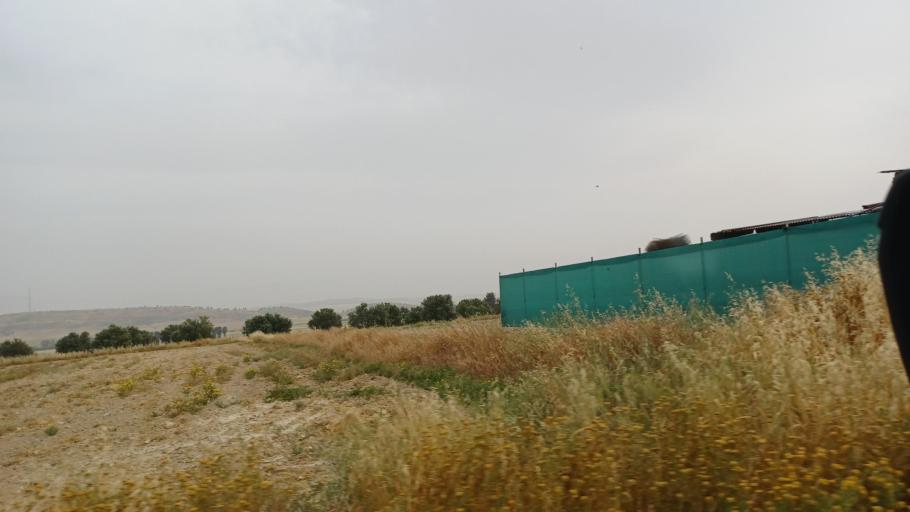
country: CY
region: Lefkosia
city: Mammari
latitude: 35.1775
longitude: 33.1974
